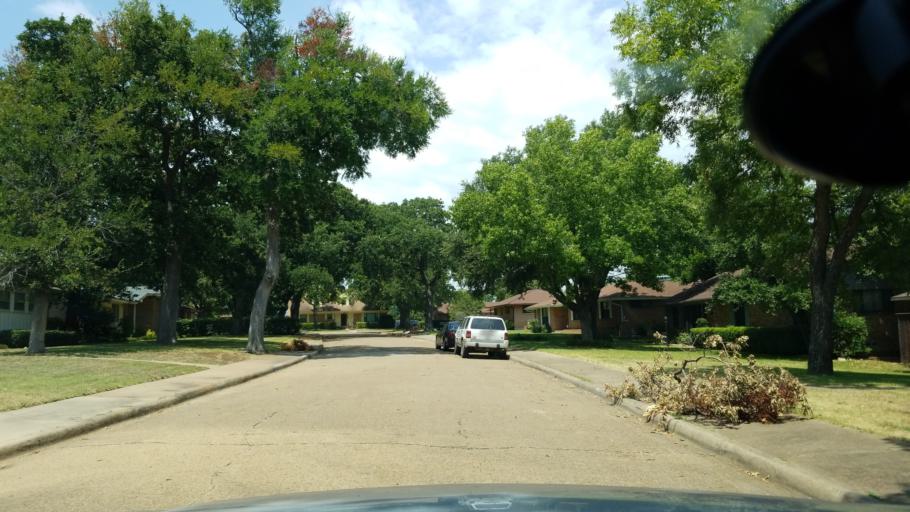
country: US
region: Texas
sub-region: Dallas County
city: Duncanville
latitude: 32.6773
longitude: -96.8382
